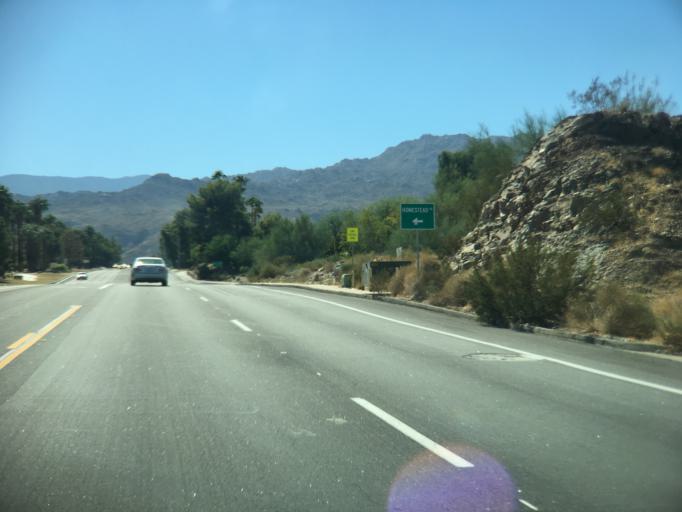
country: US
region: California
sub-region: Riverside County
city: Palm Desert
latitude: 33.7006
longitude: -116.3982
